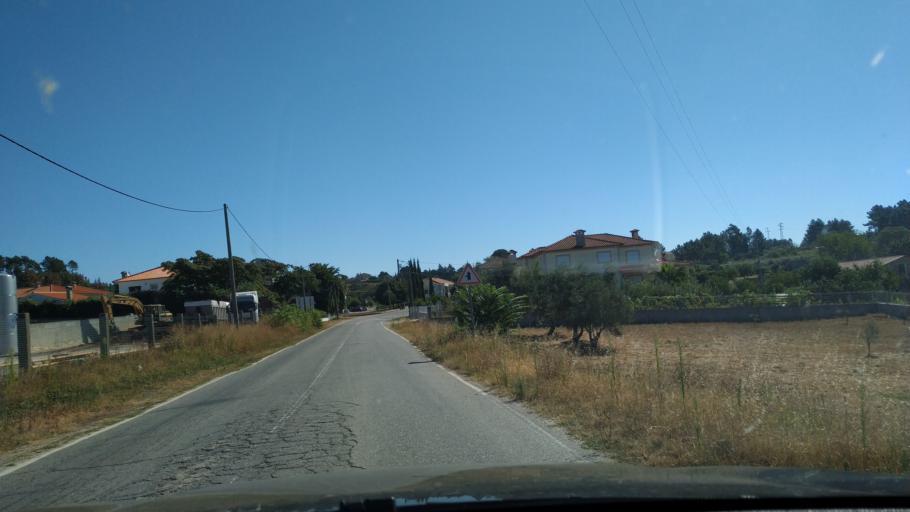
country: PT
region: Vila Real
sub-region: Sabrosa
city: Vilela
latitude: 41.2677
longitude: -7.6310
